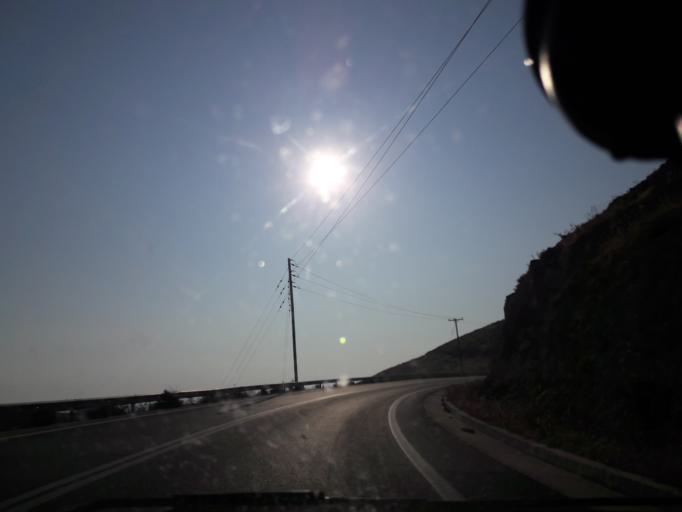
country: GR
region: North Aegean
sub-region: Nomos Lesvou
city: Myrina
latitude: 39.8616
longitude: 25.0574
